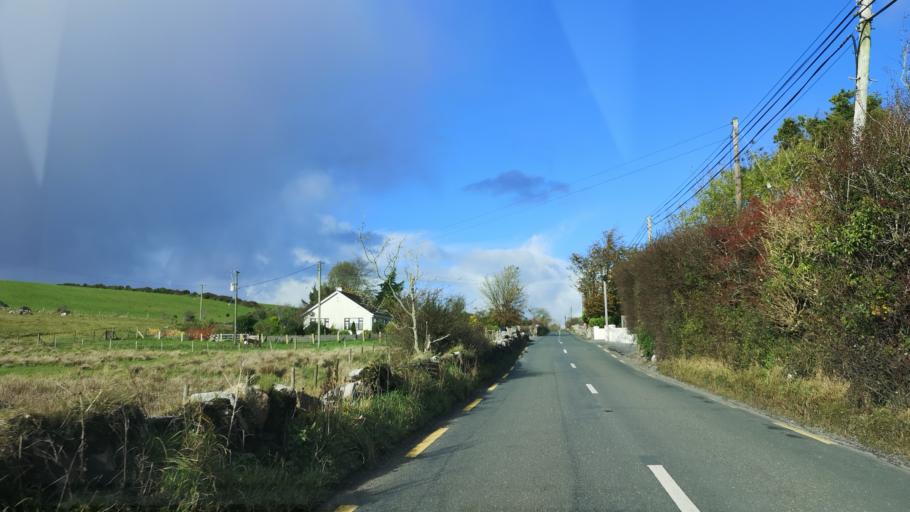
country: IE
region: Connaught
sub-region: Maigh Eo
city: Castlebar
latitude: 53.7677
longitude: -9.3828
